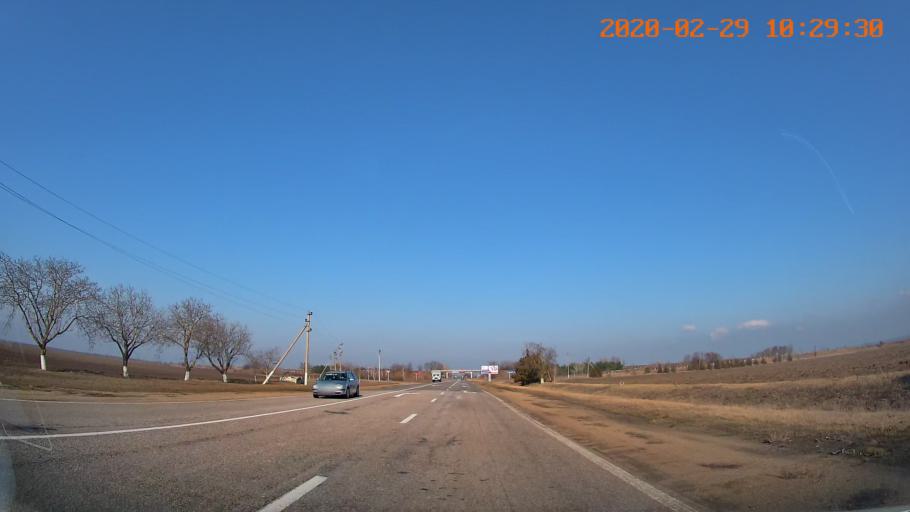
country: MD
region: Telenesti
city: Tiraspolul Nou
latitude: 46.9242
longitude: 29.5851
